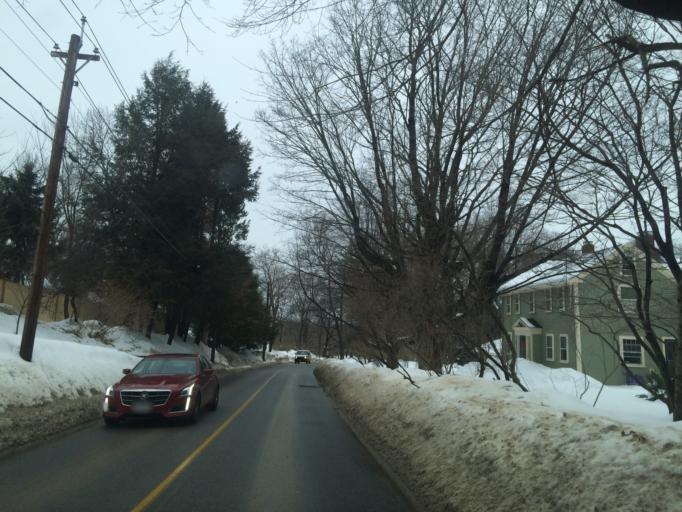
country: US
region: Massachusetts
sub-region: Middlesex County
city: Lincoln
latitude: 42.4316
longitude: -71.3014
